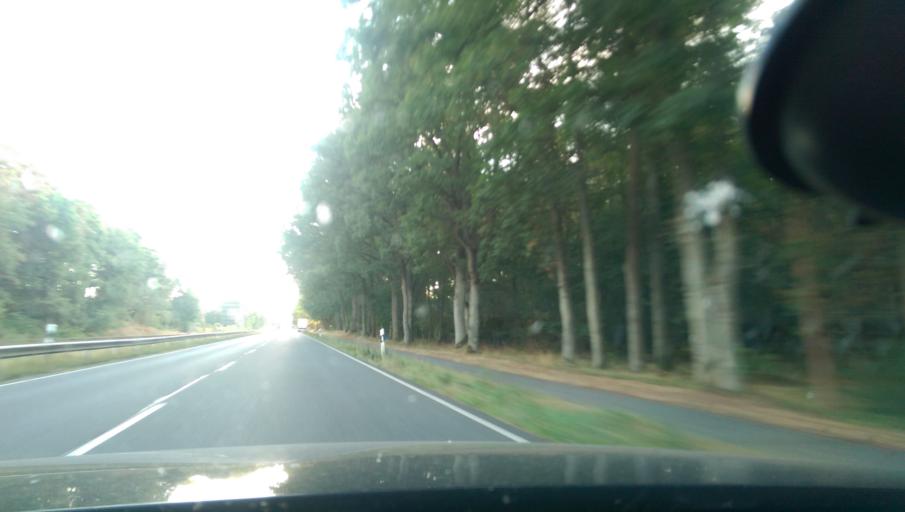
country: DE
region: Lower Saxony
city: Walsrode
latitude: 52.8317
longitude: 9.5939
